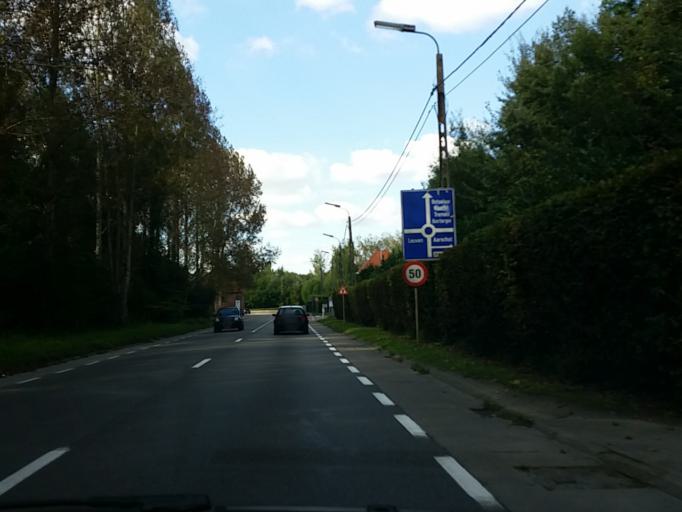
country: BE
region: Flanders
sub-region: Provincie Vlaams-Brabant
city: Holsbeek
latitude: 50.9372
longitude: 4.7395
